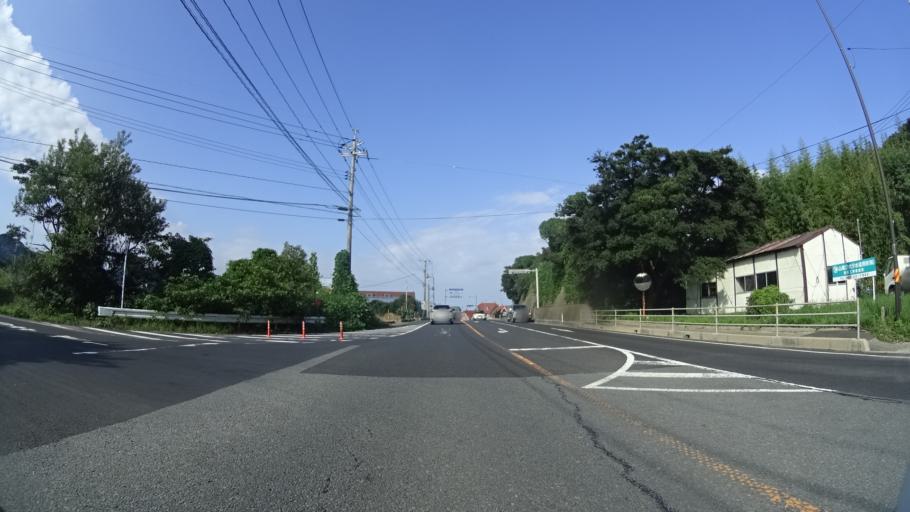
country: JP
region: Shimane
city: Izumo
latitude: 35.2911
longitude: 132.6357
